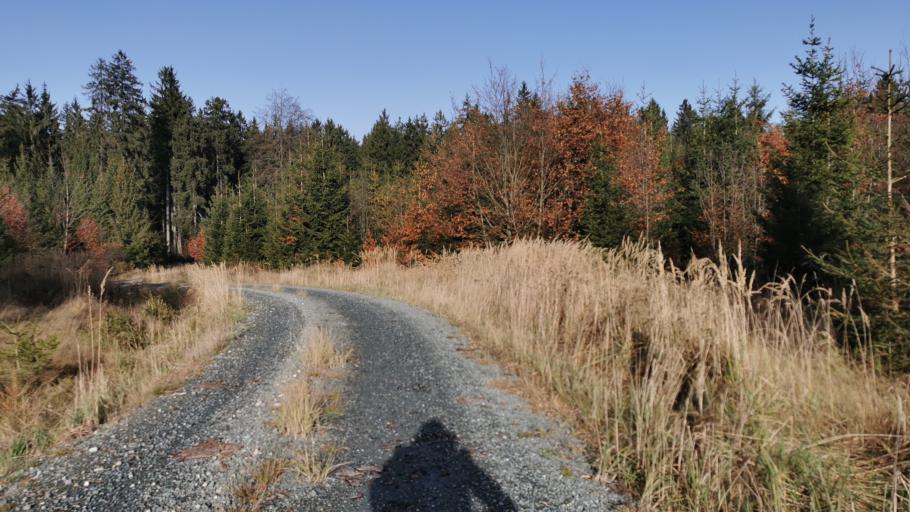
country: DE
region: Bavaria
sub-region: Upper Franconia
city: Tschirn
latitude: 50.4393
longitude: 11.4608
